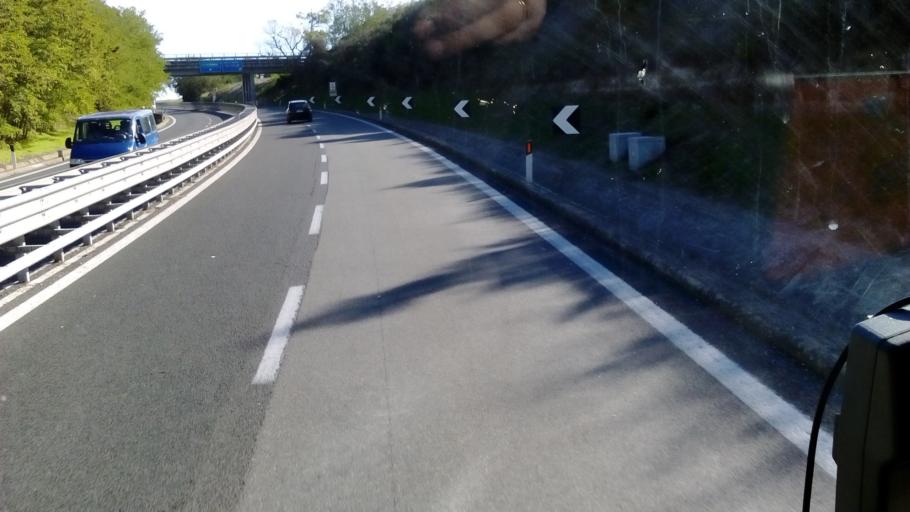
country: IT
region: Latium
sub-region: Provincia di Viterbo
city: Montalto di Castro
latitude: 42.3115
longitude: 11.6538
